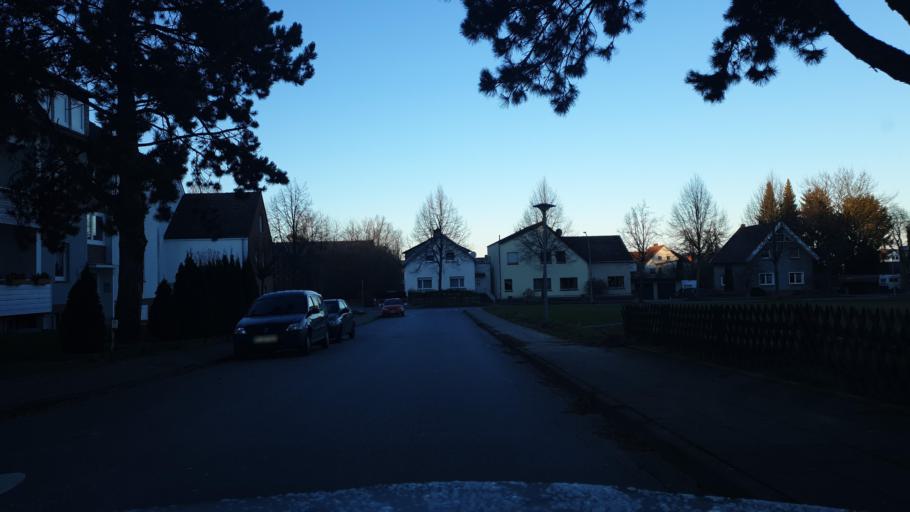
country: DE
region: North Rhine-Westphalia
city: Bad Oeynhausen
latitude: 52.1943
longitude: 8.8072
